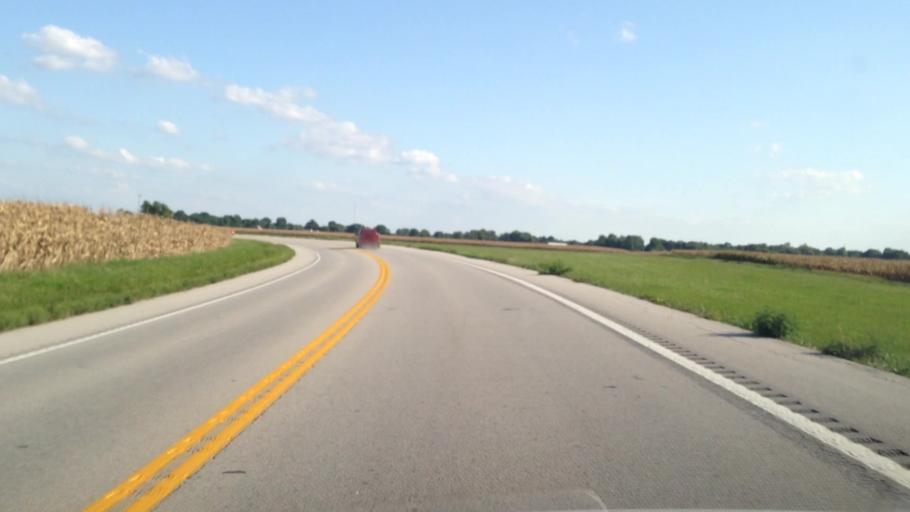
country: US
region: Missouri
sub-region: Jasper County
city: Carl Junction
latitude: 37.2863
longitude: -94.6075
